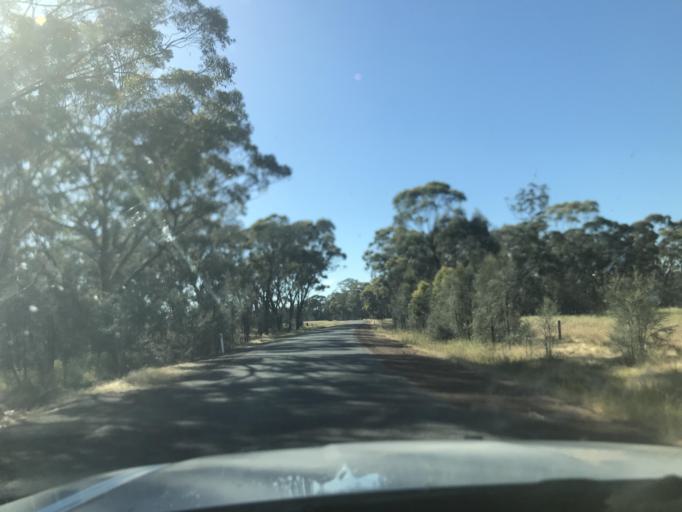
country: AU
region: Victoria
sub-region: Horsham
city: Horsham
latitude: -37.0092
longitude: 141.6596
